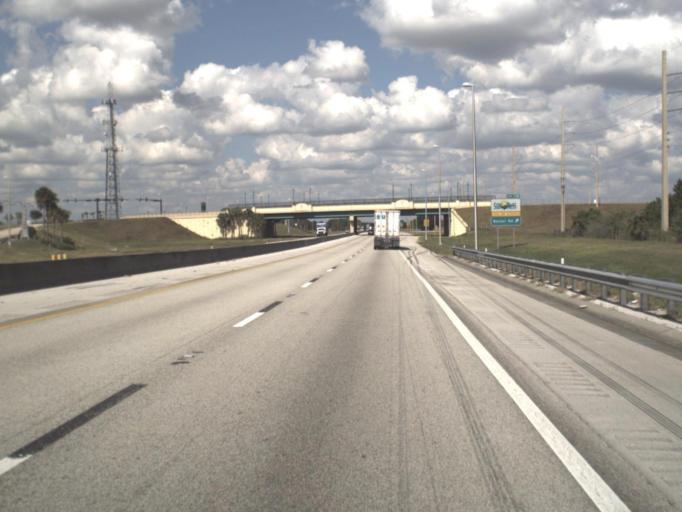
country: US
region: Florida
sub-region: Martin County
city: North River Shores
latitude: 27.2072
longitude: -80.3324
